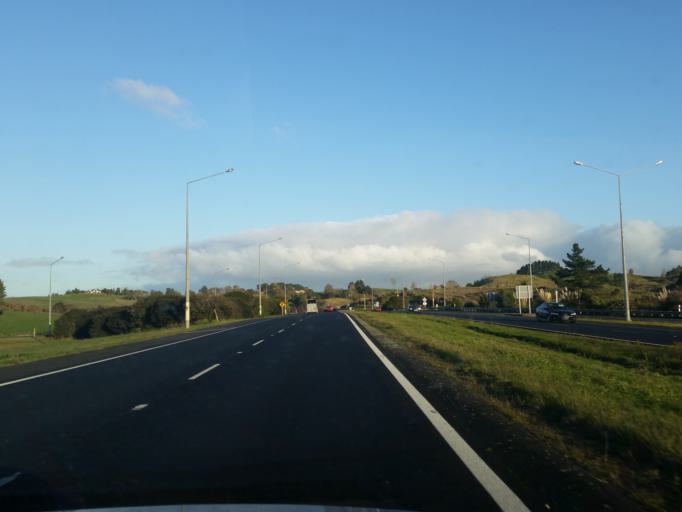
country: NZ
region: Auckland
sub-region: Auckland
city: Pukekohe East
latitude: -37.2485
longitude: 175.0282
